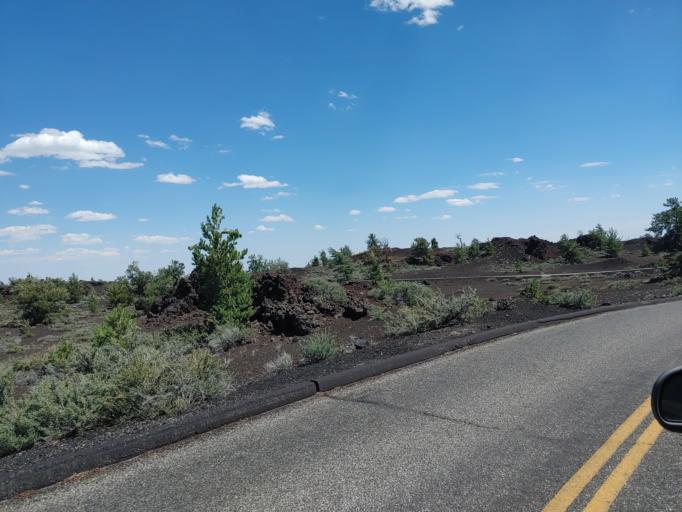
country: US
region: Idaho
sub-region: Butte County
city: Arco
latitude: 43.4527
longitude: -113.5438
